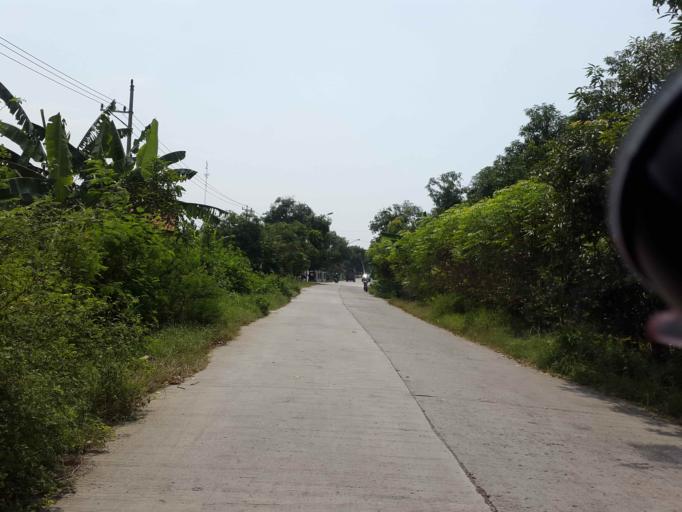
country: ID
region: Central Java
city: Pemalang
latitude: -6.9080
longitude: 109.4003
